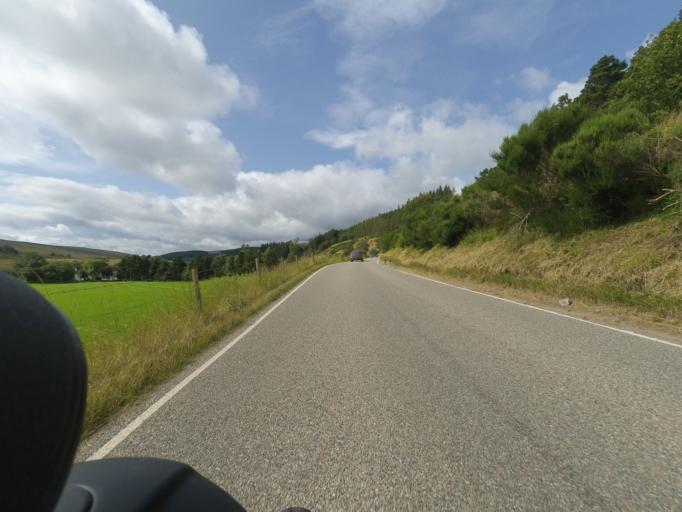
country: GB
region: Scotland
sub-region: Highland
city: Grantown on Spey
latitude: 57.2581
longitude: -3.3902
